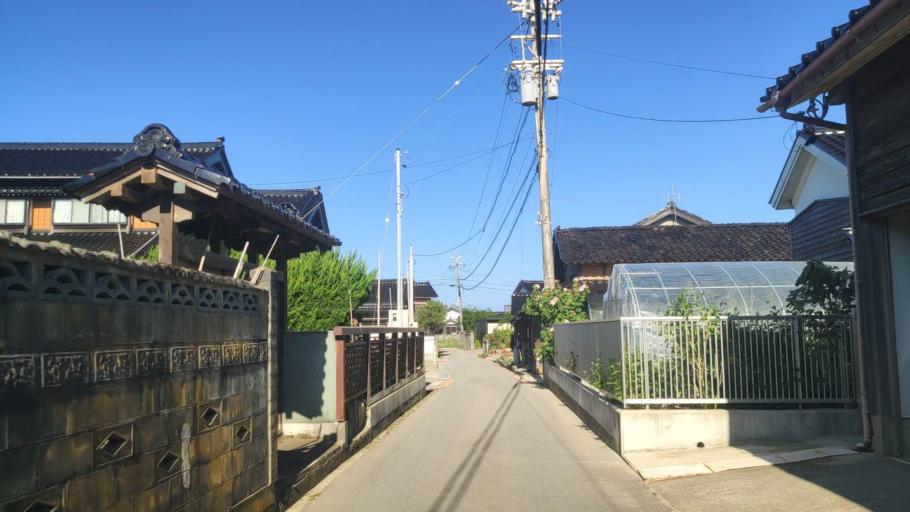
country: JP
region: Ishikawa
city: Hakui
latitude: 36.9504
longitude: 136.7635
